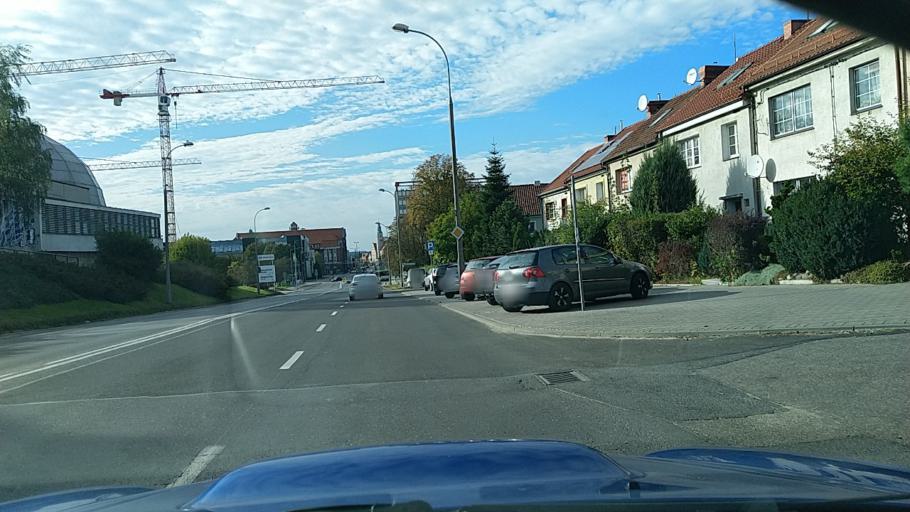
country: PL
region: Warmian-Masurian Voivodeship
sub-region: Powiat olsztynski
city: Olsztyn
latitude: 53.7753
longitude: 20.4925
